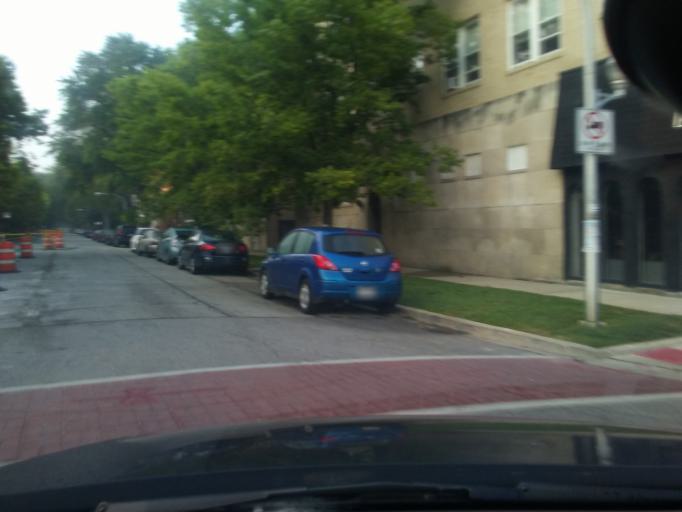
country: US
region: Illinois
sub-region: Cook County
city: Lincolnwood
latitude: 41.9540
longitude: -87.6848
